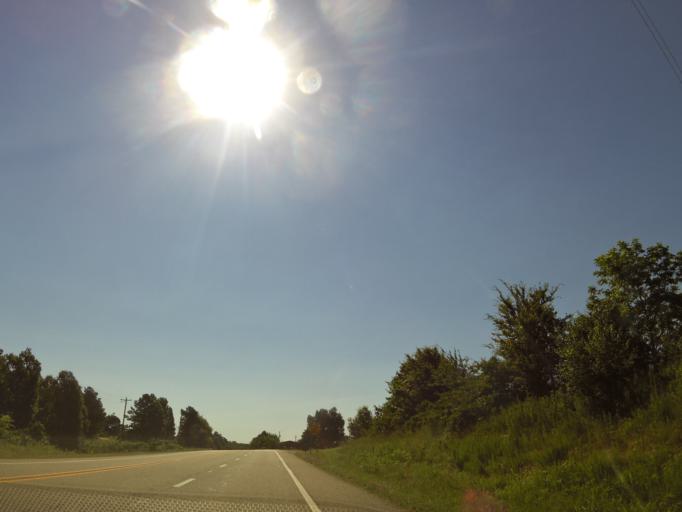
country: US
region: Arkansas
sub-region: Clay County
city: Piggott
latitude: 36.4336
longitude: -90.3164
